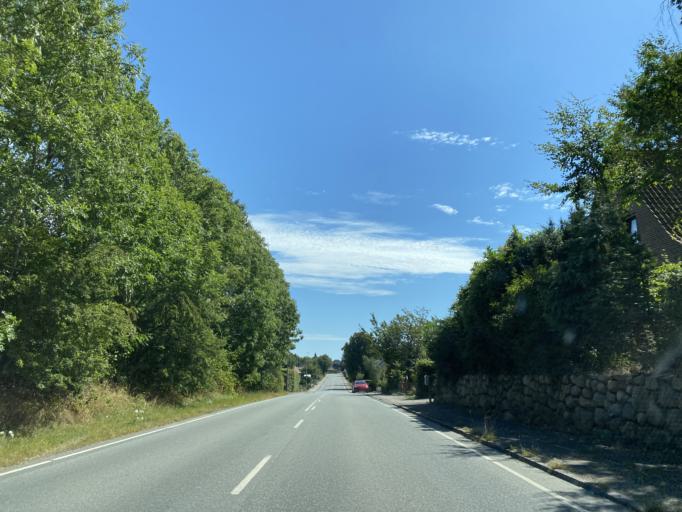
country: DK
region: South Denmark
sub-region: Faaborg-Midtfyn Kommune
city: Ringe
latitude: 55.2388
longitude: 10.5594
